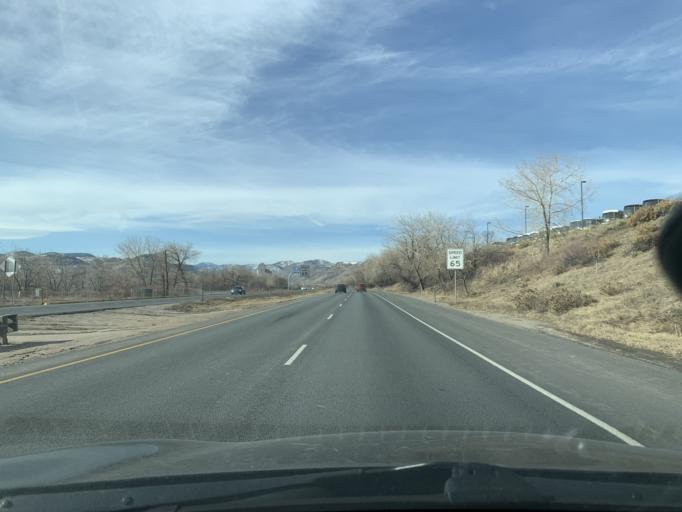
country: US
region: Colorado
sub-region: Jefferson County
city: Applewood
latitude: 39.7751
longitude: -105.1566
